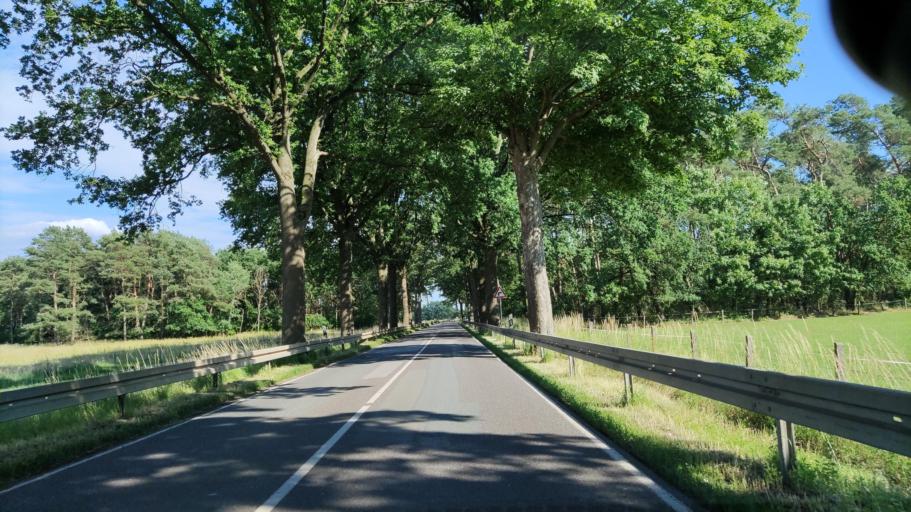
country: DE
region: Mecklenburg-Vorpommern
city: Domitz
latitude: 53.1674
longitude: 11.2361
